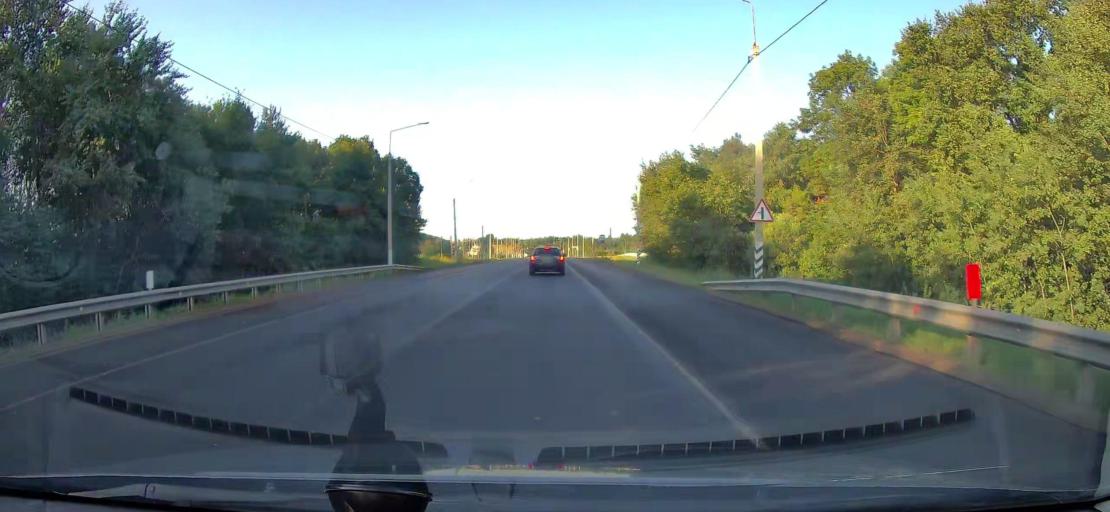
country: RU
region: Tula
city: Pervomayskiy
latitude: 54.0139
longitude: 37.4807
